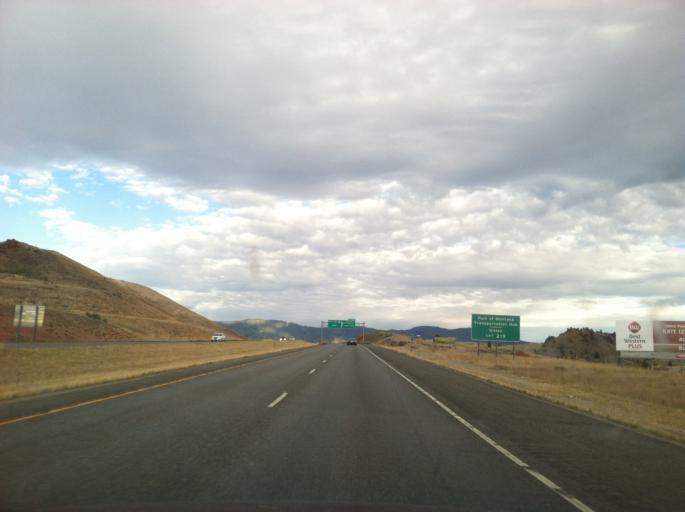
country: US
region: Montana
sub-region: Silver Bow County
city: Butte-Silver Bow (Balance)
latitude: 46.0073
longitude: -112.6594
